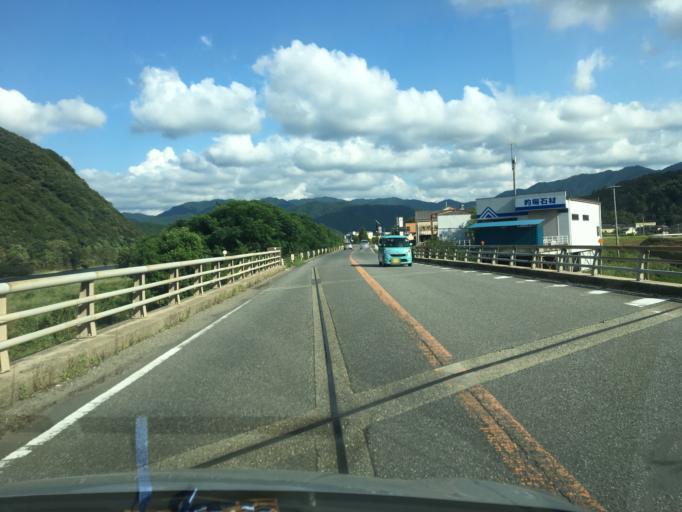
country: JP
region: Hyogo
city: Toyooka
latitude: 35.4438
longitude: 134.7756
